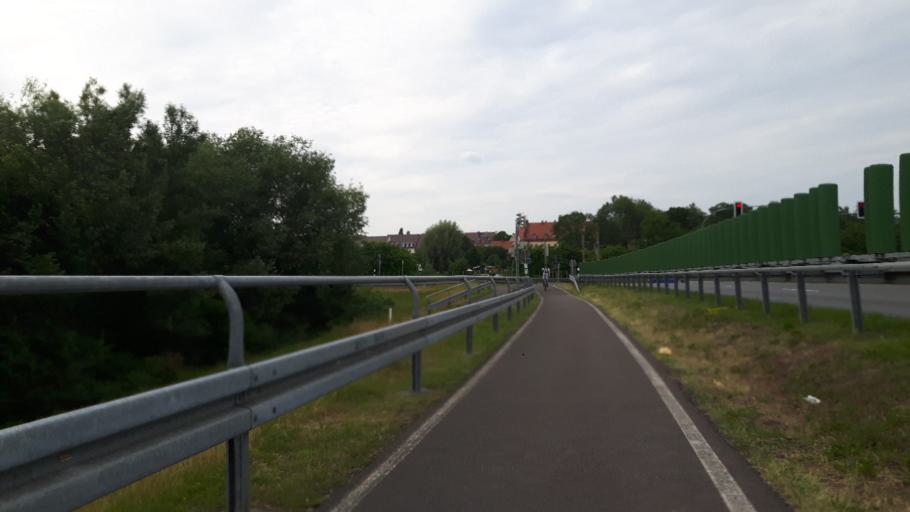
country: DE
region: Saxony-Anhalt
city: Wittenburg
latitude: 51.8608
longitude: 12.6522
